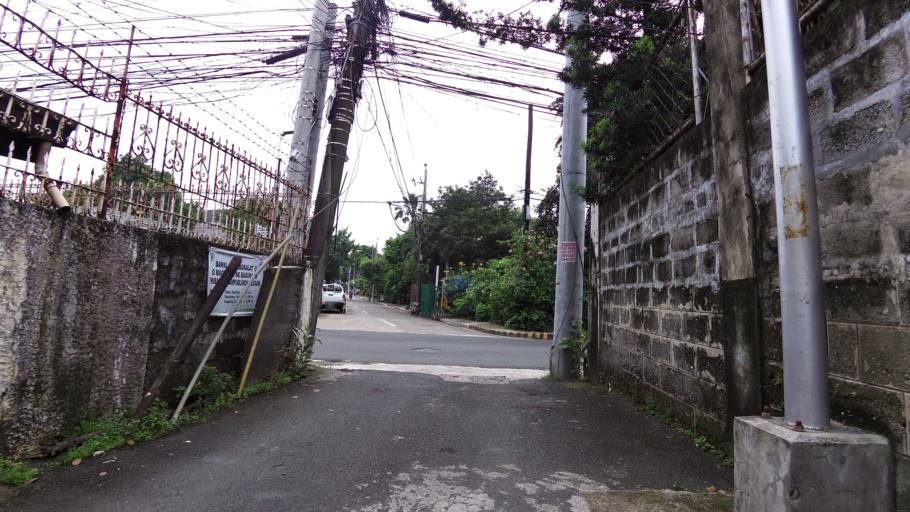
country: PH
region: Metro Manila
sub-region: Quezon City
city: Quezon City
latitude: 14.6373
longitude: 121.0579
